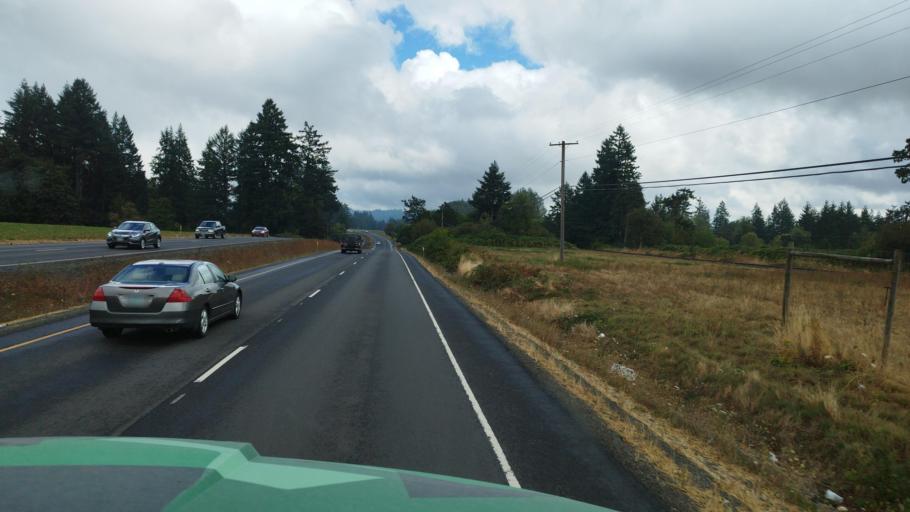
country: US
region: Oregon
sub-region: Yamhill County
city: Lafayette
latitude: 45.2406
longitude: -123.1381
